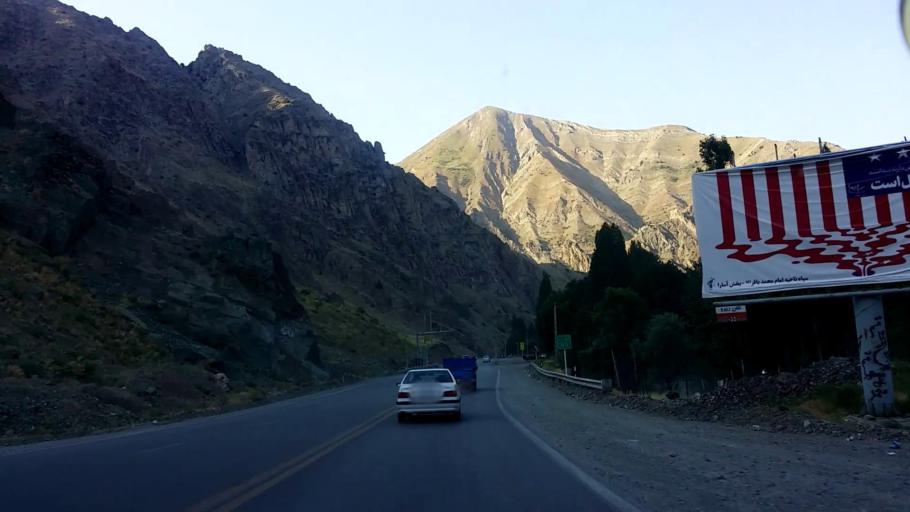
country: IR
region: Tehran
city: Tajrish
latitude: 36.0351
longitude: 51.3132
